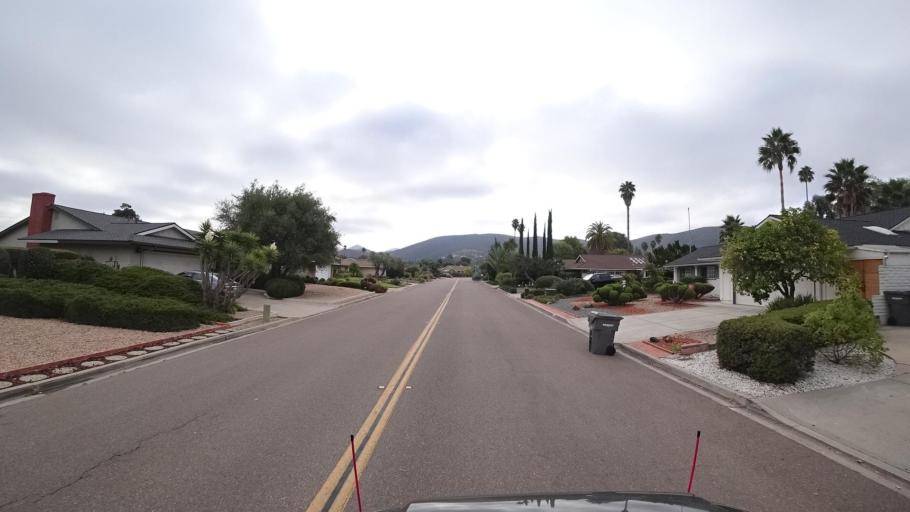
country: US
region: California
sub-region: San Diego County
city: Lake San Marcos
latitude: 33.1274
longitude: -117.1990
